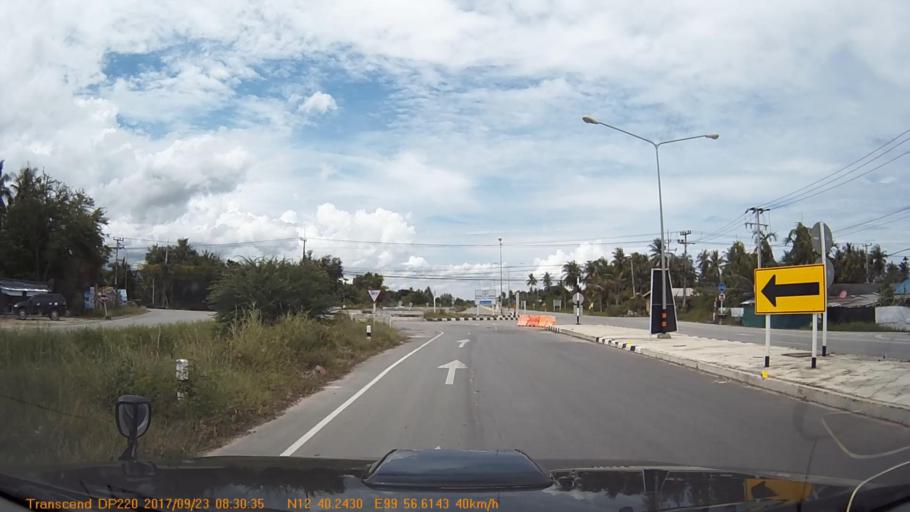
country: TH
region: Prachuap Khiri Khan
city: Hua Hin
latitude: 12.6710
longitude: 99.9434
